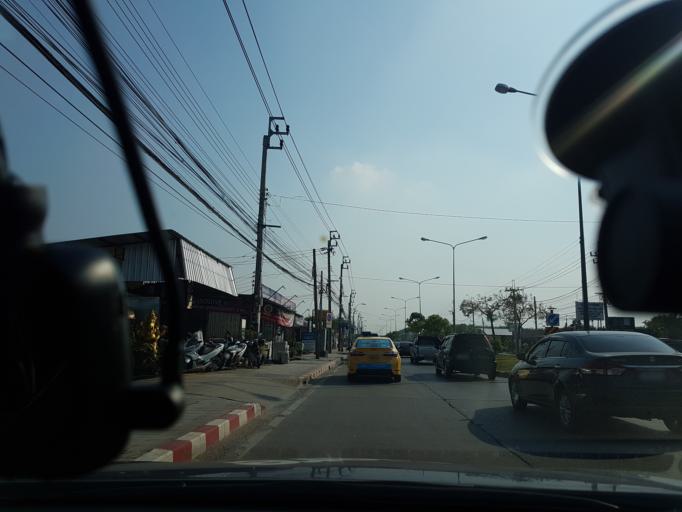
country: TH
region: Bangkok
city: Khlong Sam Wa
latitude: 13.8708
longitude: 100.7226
